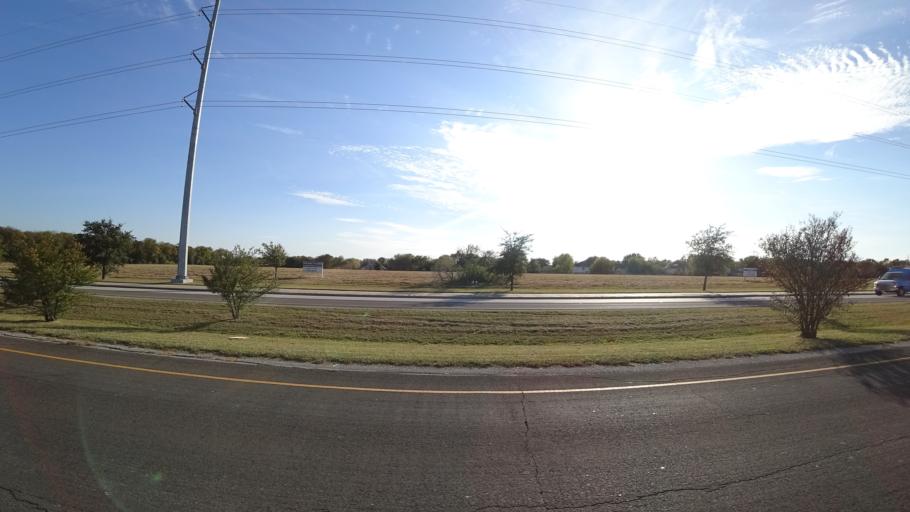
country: US
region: Texas
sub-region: Travis County
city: Pflugerville
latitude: 30.4076
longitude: -97.6443
